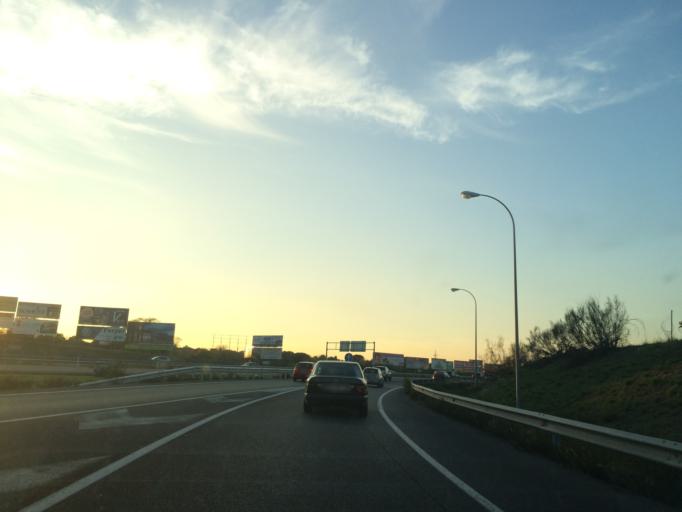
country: ES
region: Madrid
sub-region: Provincia de Madrid
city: Pozuelo de Alarcon
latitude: 40.4332
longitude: -3.8371
